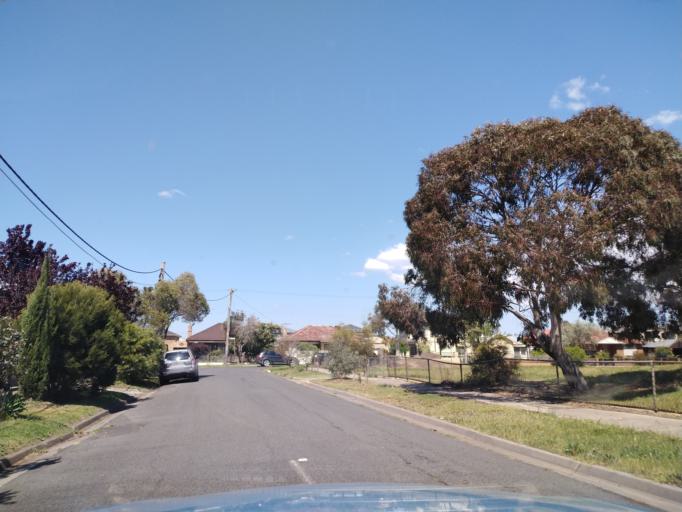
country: AU
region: Victoria
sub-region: Hobsons Bay
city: Altona North
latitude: -37.8372
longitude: 144.8599
